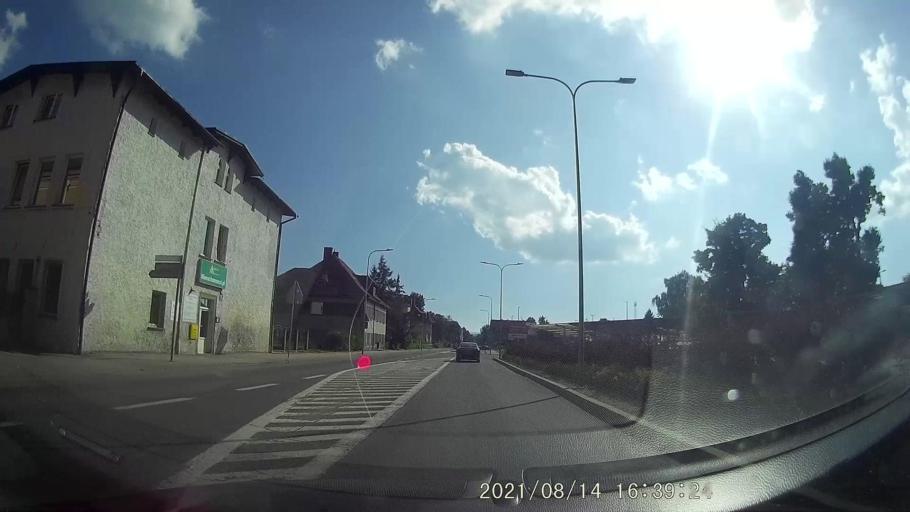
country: PL
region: Lower Silesian Voivodeship
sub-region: Powiat kamiennogorski
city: Kamienna Gora
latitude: 50.7848
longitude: 16.0232
